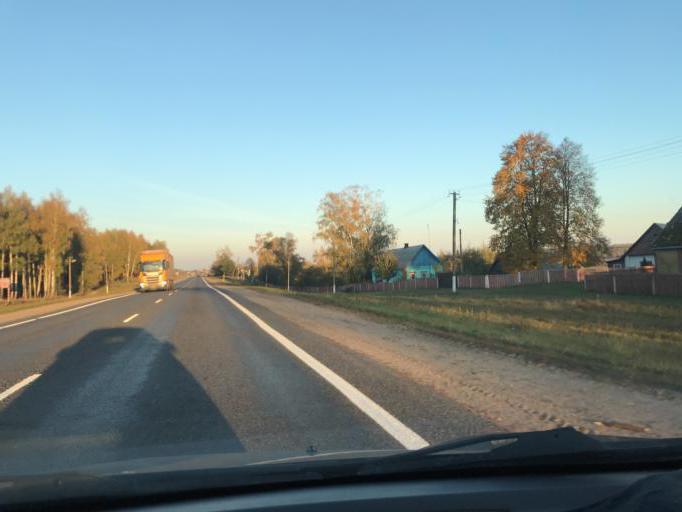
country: BY
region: Minsk
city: Staryya Darohi
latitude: 53.0510
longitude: 28.3886
